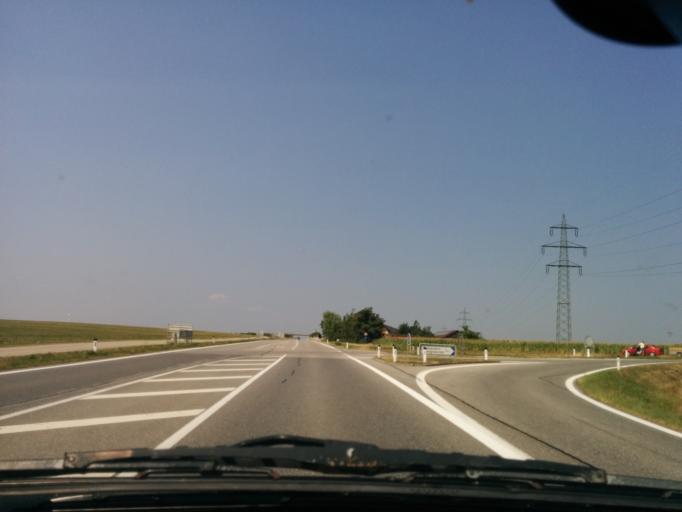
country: AT
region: Lower Austria
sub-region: Politischer Bezirk Krems
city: Jaidhof
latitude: 48.5255
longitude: 15.4758
